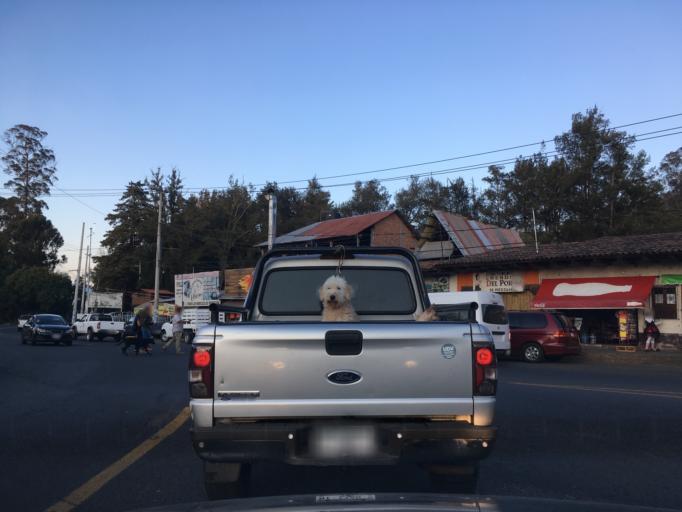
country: MX
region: Michoacan
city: Patzcuaro
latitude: 19.5393
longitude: -101.6121
